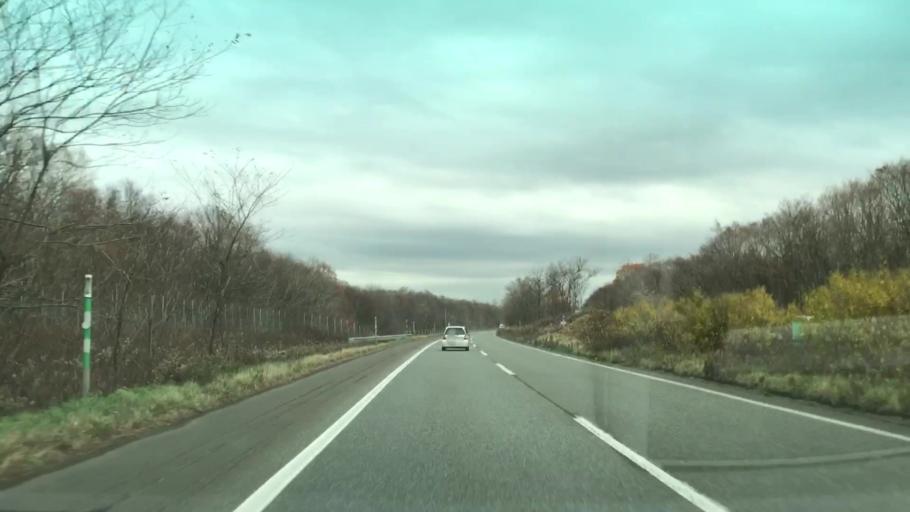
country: JP
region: Hokkaido
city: Chitose
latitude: 42.7996
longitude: 141.6261
